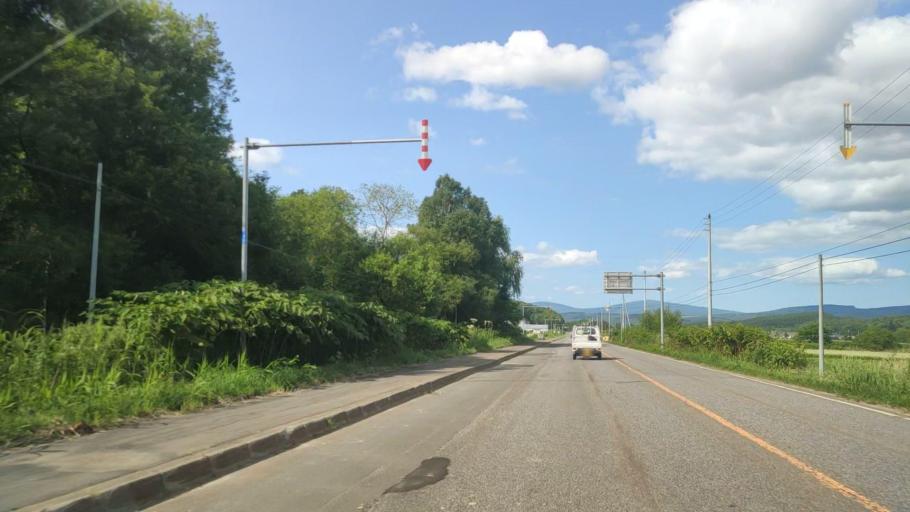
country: JP
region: Hokkaido
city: Nayoro
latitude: 44.3977
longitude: 142.3949
